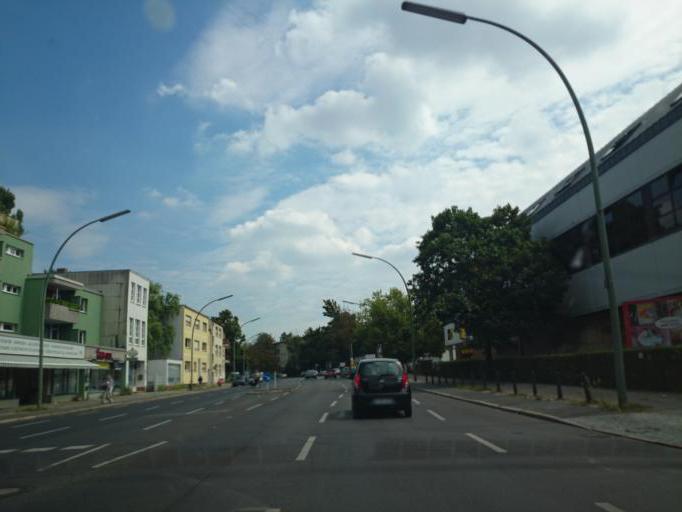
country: DE
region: Berlin
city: Lankwitz
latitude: 52.4301
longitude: 13.3340
